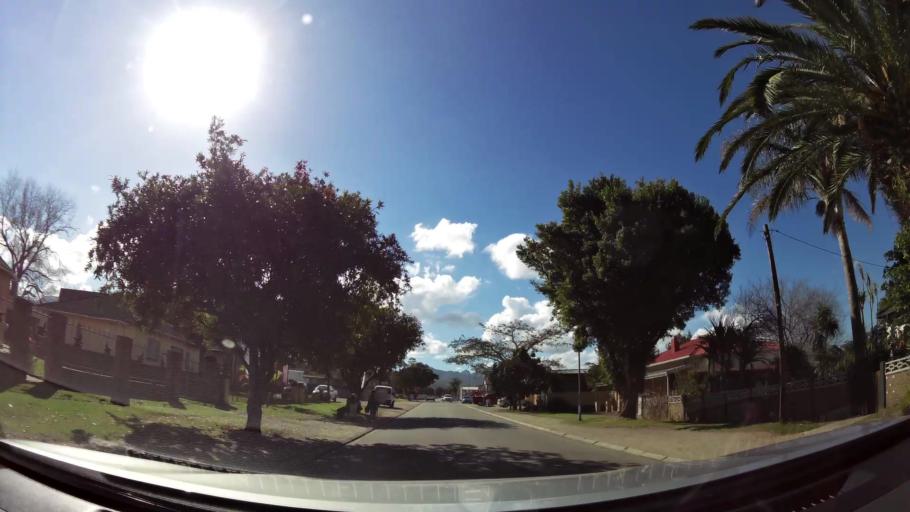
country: ZA
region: Western Cape
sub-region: Eden District Municipality
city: George
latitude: -33.9659
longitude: 22.4637
